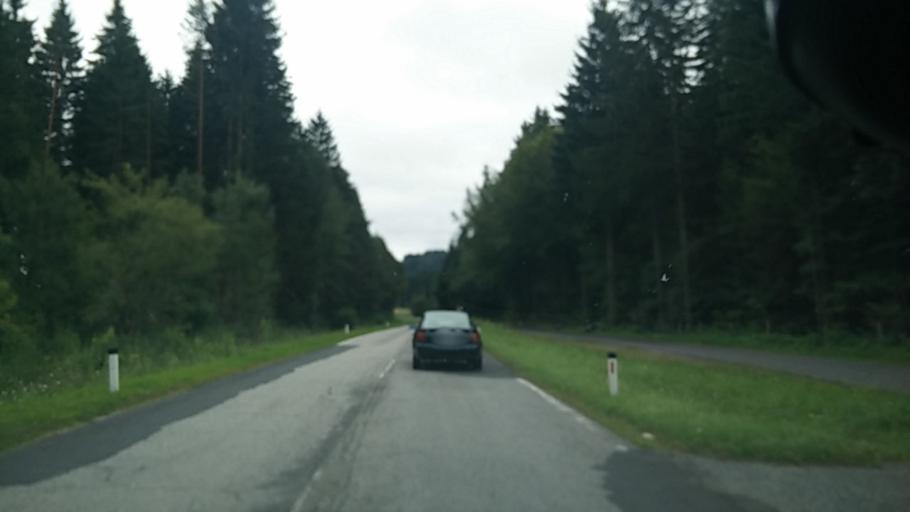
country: AT
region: Carinthia
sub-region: Politischer Bezirk Villach Land
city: Rosegg
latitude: 46.5506
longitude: 13.9984
